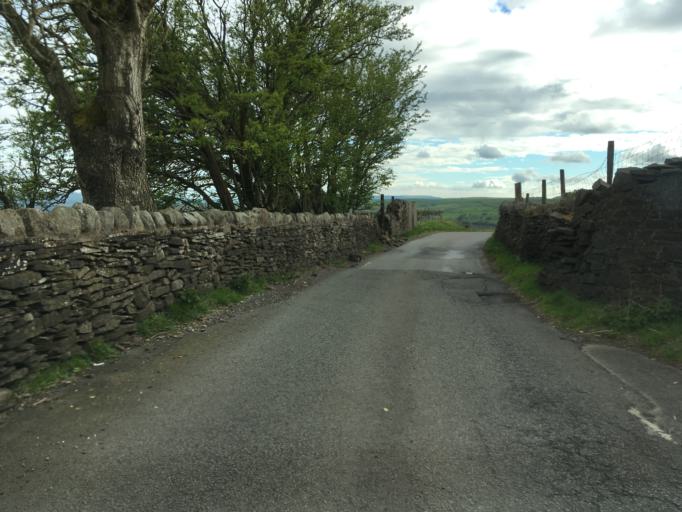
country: GB
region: Wales
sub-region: Merthyr Tydfil County Borough
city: Treharris
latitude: 51.7136
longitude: -3.3084
